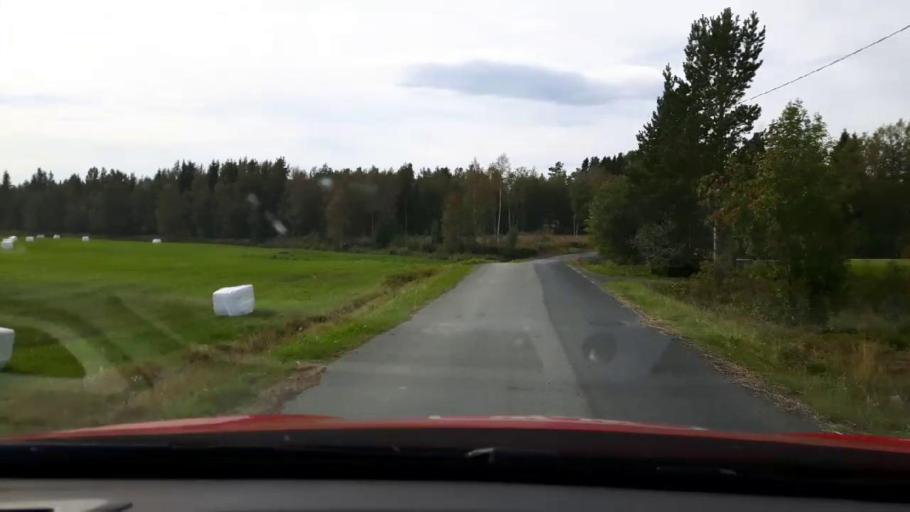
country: SE
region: Jaemtland
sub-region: Krokoms Kommun
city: Valla
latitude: 63.2635
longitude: 13.8484
